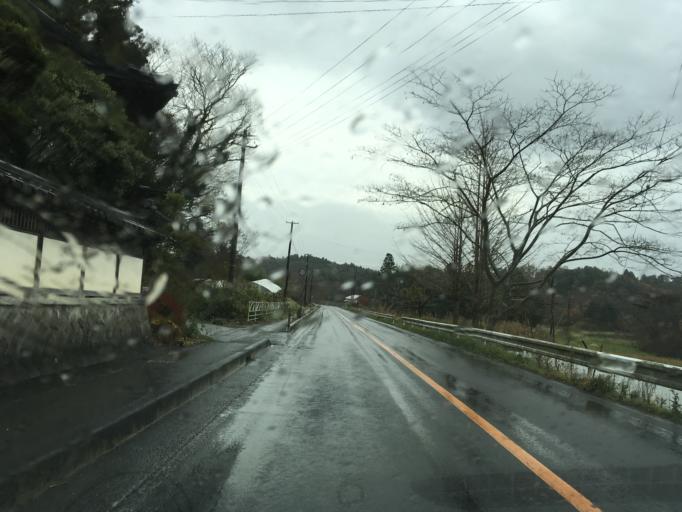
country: JP
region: Iwate
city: Ichinoseki
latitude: 38.7710
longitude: 141.2448
